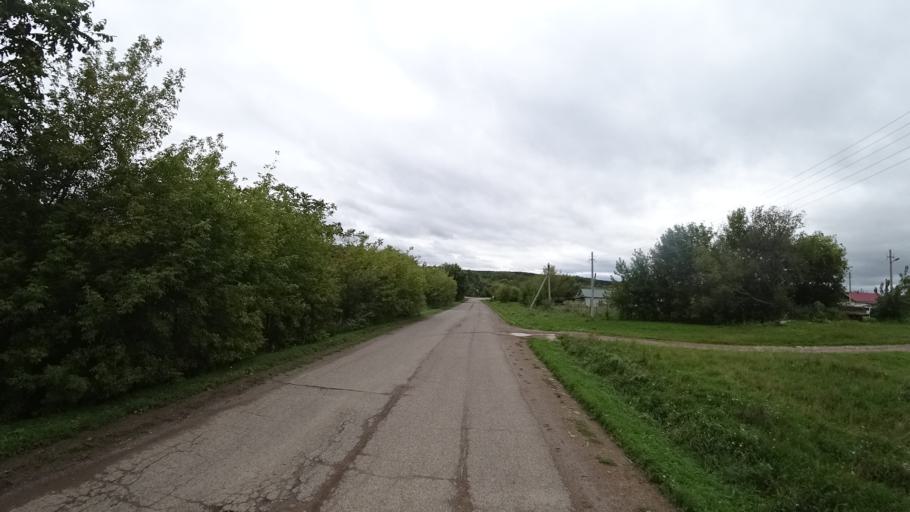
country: RU
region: Primorskiy
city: Chernigovka
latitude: 44.4627
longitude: 132.5910
